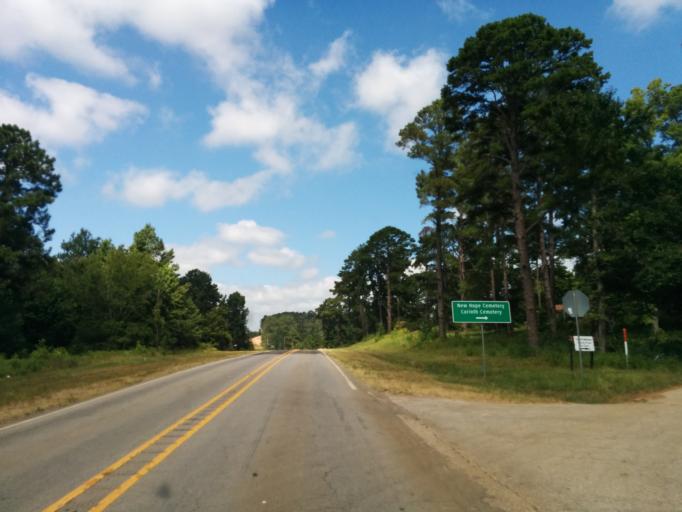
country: US
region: Texas
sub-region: Houston County
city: Hickory Creek
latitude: 31.3587
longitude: -95.1955
